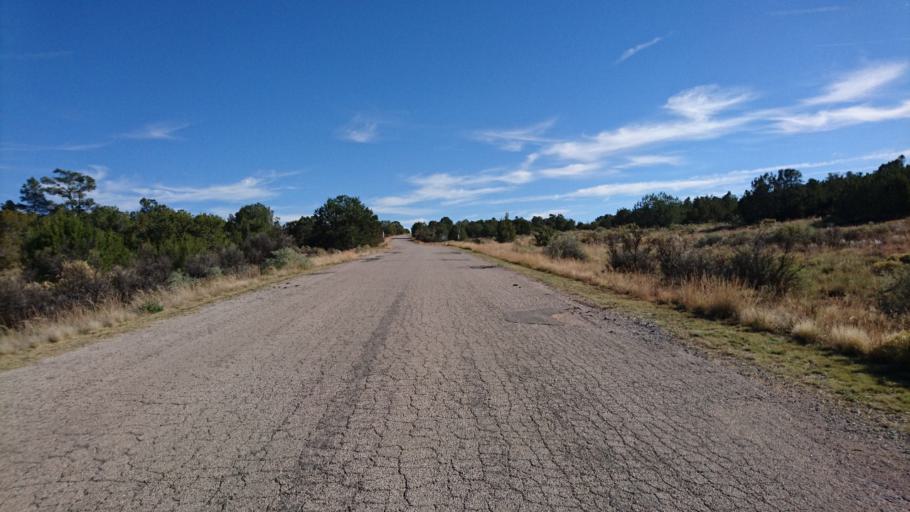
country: US
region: Arizona
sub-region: Mohave County
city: Peach Springs
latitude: 35.5217
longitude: -113.2265
